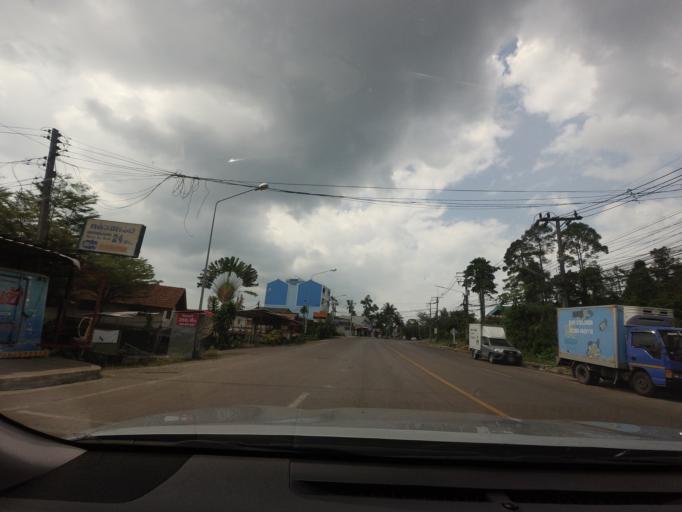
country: TH
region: Phangnga
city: Ban Ao Nang
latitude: 8.0532
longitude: 98.7583
